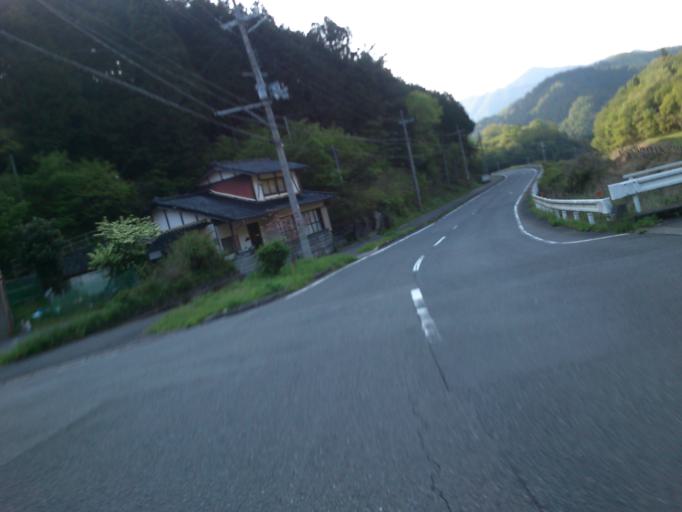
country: JP
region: Kyoto
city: Fukuchiyama
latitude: 35.3200
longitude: 135.0602
